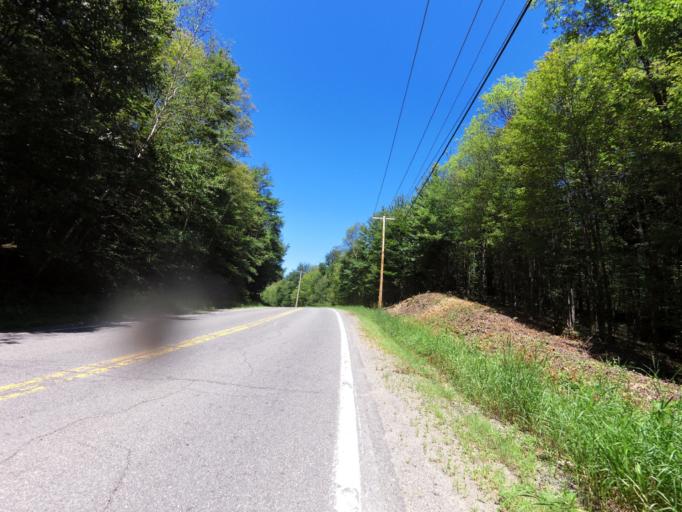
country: CA
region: Quebec
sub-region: Laurentides
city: Brownsburg-Chatham
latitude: 45.8469
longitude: -74.5570
